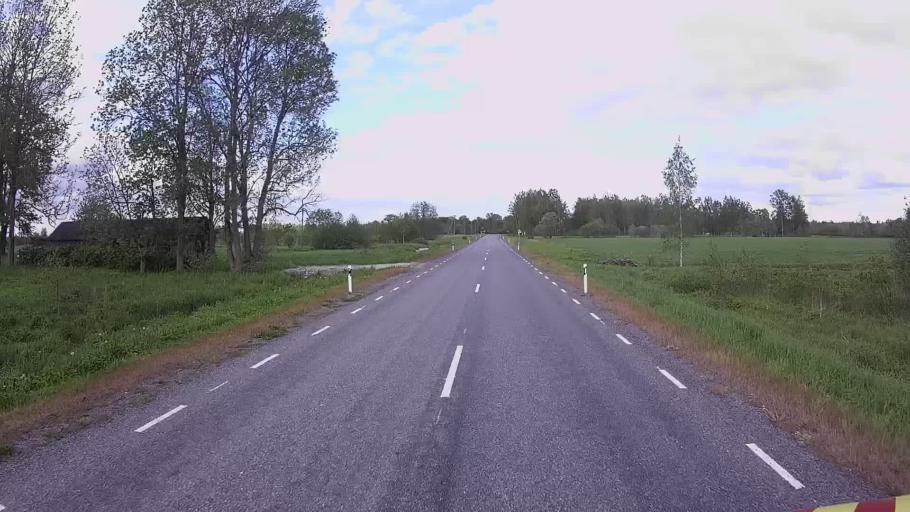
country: EE
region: Jogevamaa
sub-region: Mustvee linn
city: Mustvee
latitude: 59.0149
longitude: 26.9417
